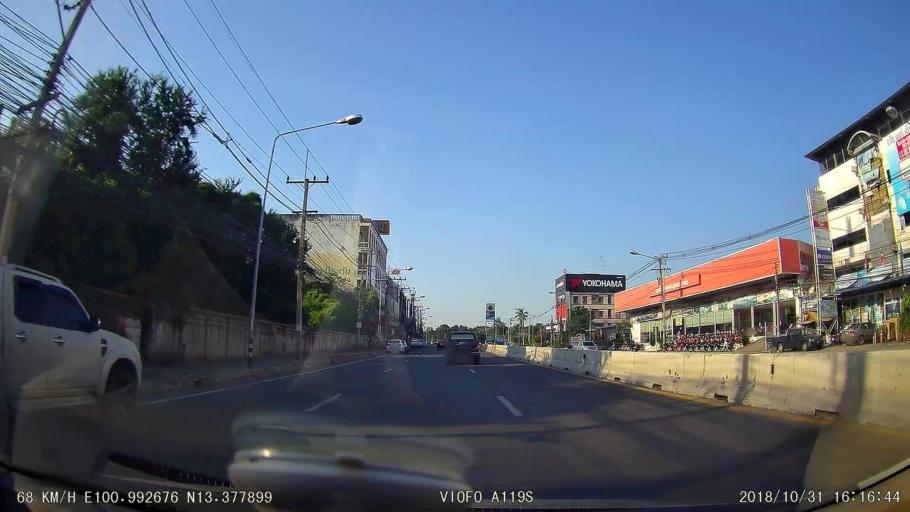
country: TH
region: Chon Buri
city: Chon Buri
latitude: 13.3782
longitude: 100.9926
